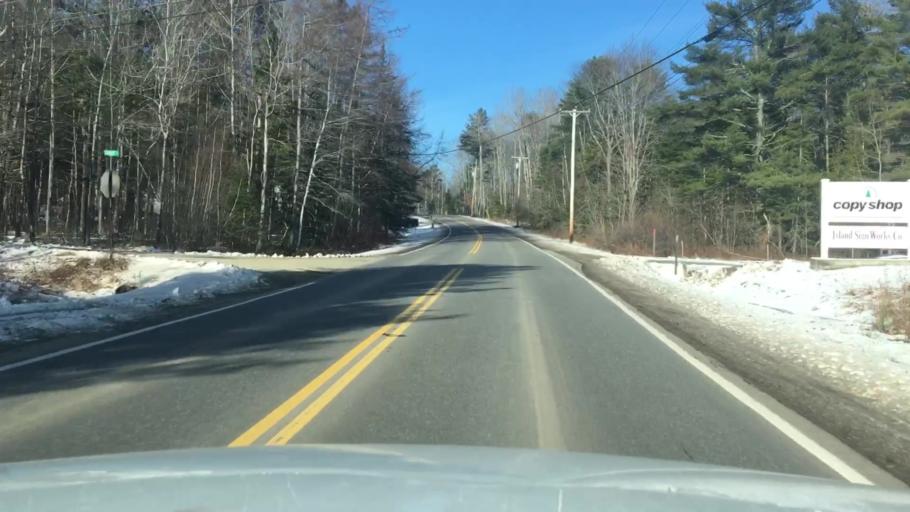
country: US
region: Maine
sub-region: Lincoln County
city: Wiscasset
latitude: 43.9679
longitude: -69.7095
